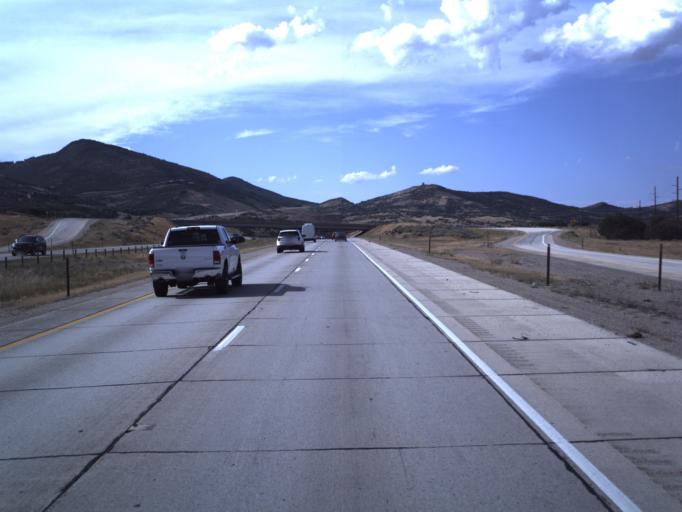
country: US
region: Utah
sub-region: Summit County
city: Park City
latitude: 40.6211
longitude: -111.4377
